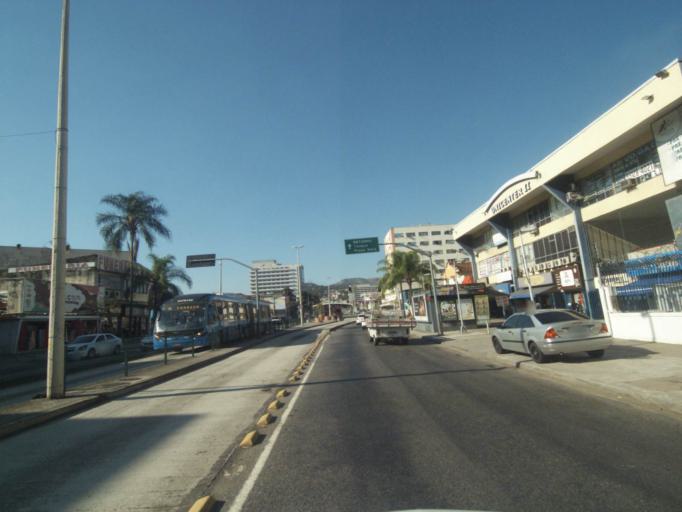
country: BR
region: Rio de Janeiro
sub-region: Sao Joao De Meriti
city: Sao Joao de Meriti
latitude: -22.9208
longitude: -43.3694
